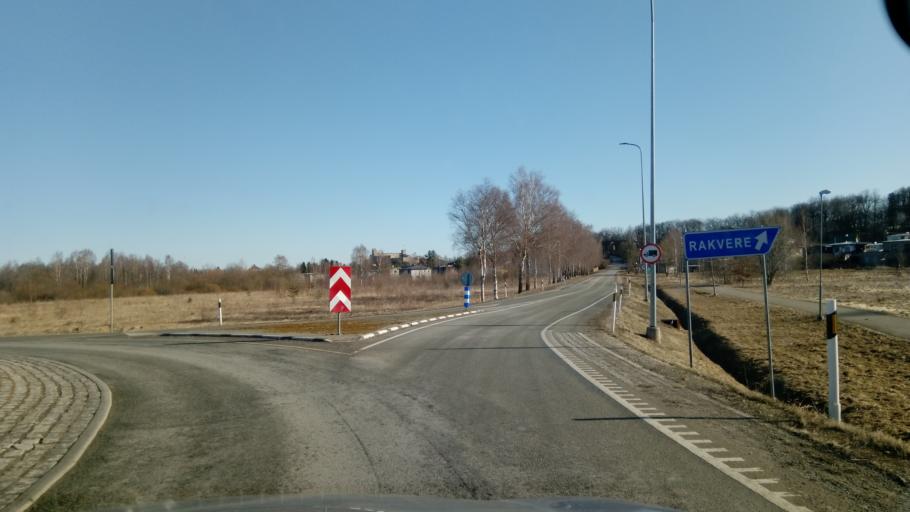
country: EE
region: Laeaene-Virumaa
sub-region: Rakvere linn
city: Rakvere
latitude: 59.3399
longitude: 26.3430
